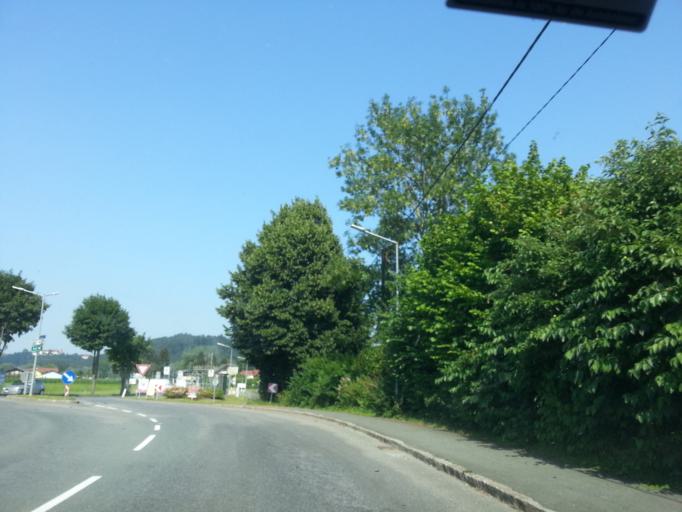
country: AT
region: Styria
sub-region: Politischer Bezirk Leibnitz
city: Heimschuh
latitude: 46.7641
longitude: 15.4947
